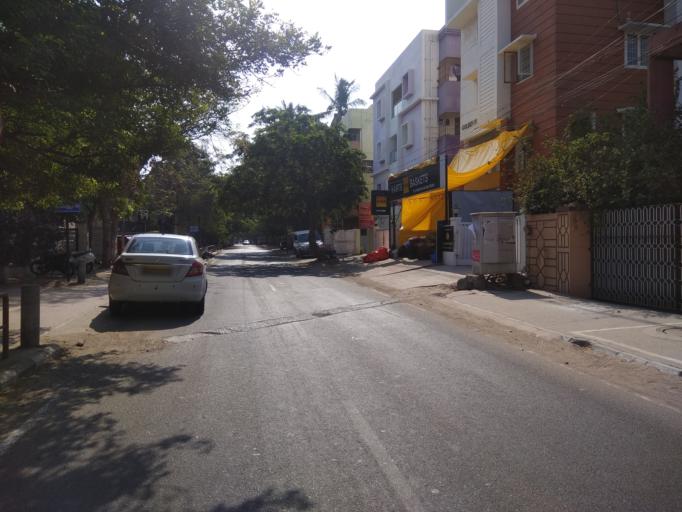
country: IN
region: Tamil Nadu
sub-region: Kancheepuram
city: Saint Thomas Mount
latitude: 13.0407
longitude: 80.2013
